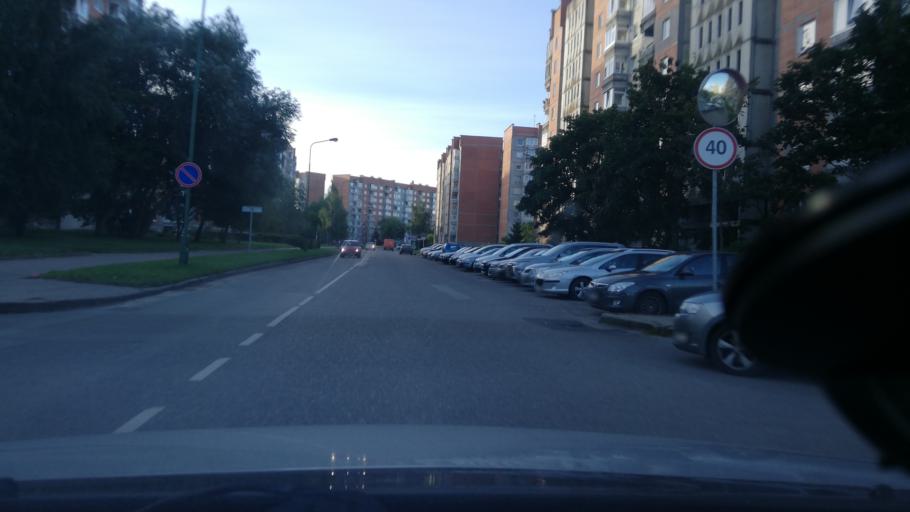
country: LT
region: Klaipedos apskritis
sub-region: Klaipeda
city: Klaipeda
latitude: 55.6693
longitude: 21.2002
